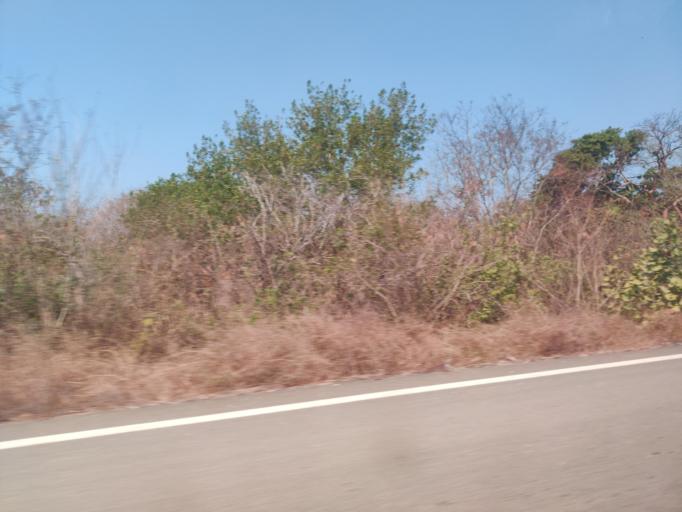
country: CO
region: Bolivar
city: Turbana
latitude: 10.1799
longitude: -75.6453
